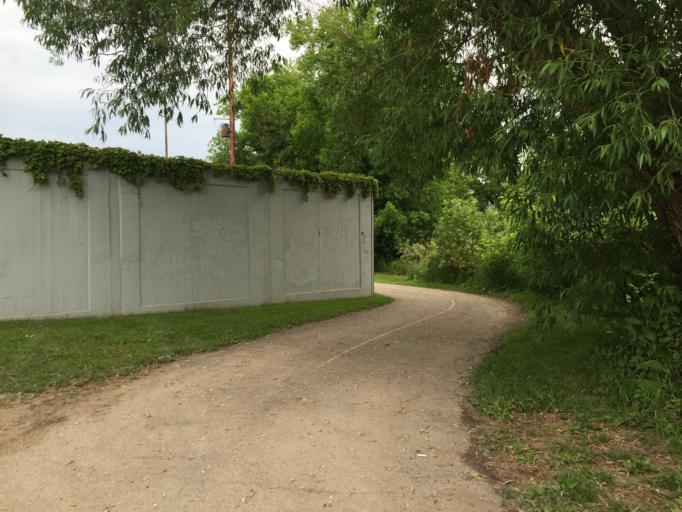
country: CA
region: Ontario
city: Oshawa
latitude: 43.8985
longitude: -78.8698
